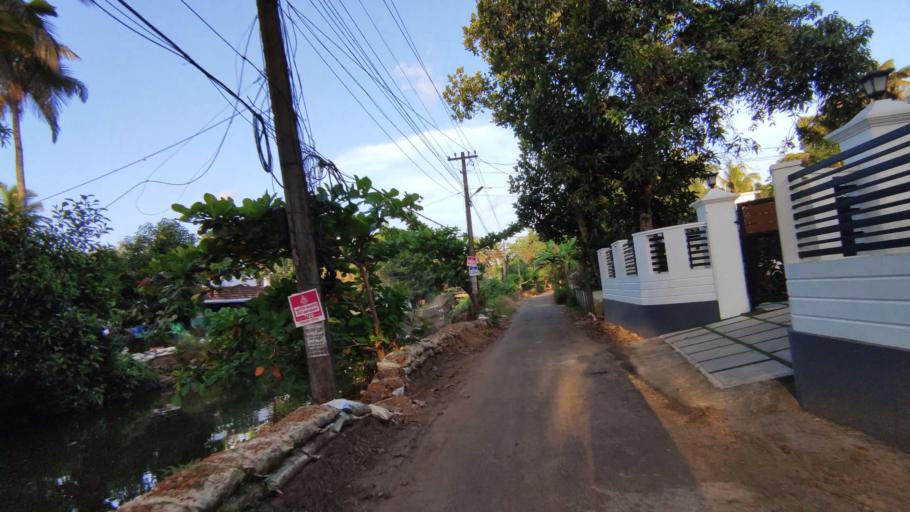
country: IN
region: Kerala
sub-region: Kottayam
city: Kottayam
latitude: 9.5958
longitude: 76.4590
